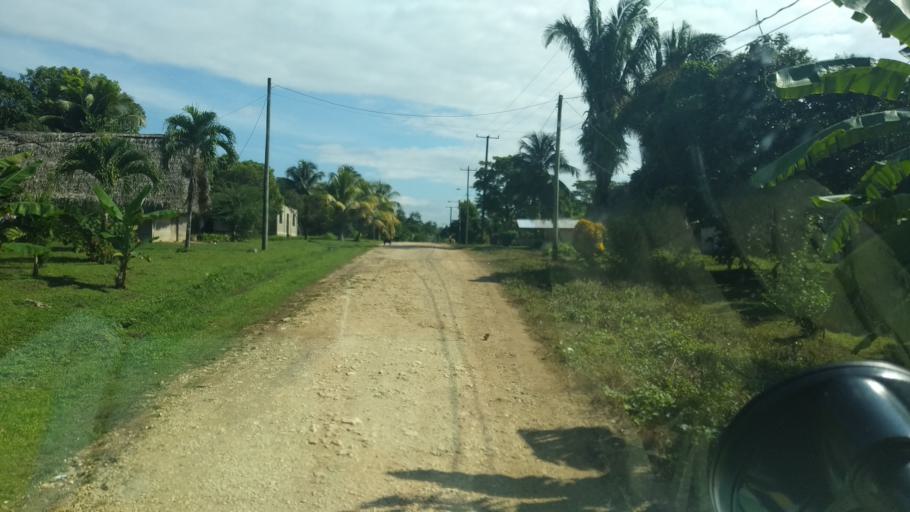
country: BZ
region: Toledo
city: Punta Gorda
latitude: 16.2154
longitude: -88.9077
